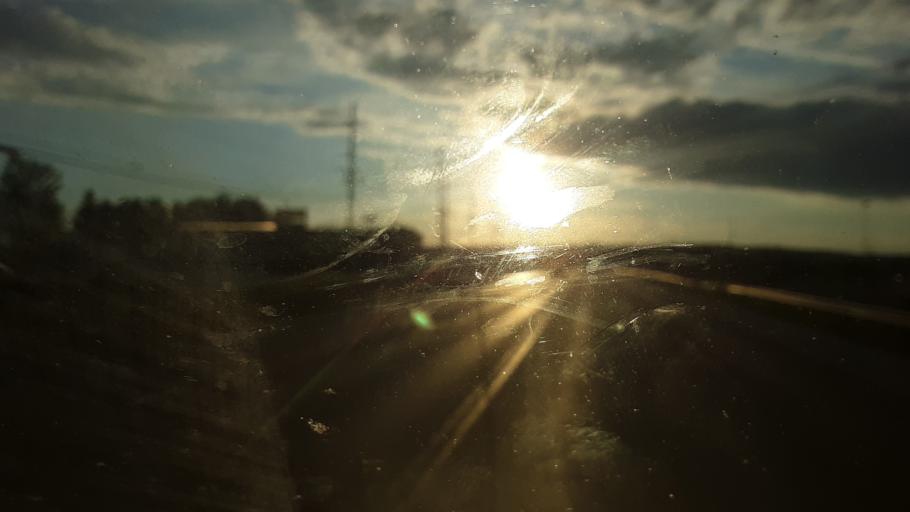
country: US
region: Maine
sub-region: Aroostook County
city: Presque Isle
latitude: 46.6992
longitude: -68.0075
